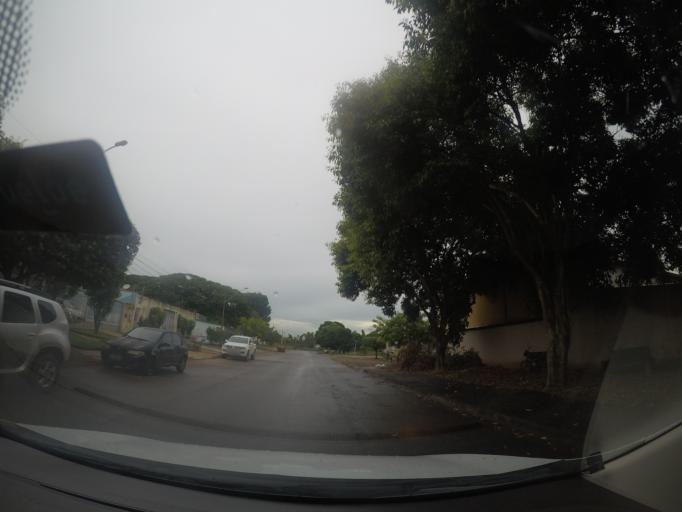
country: BR
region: Goias
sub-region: Goiania
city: Goiania
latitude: -16.6329
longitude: -49.2342
